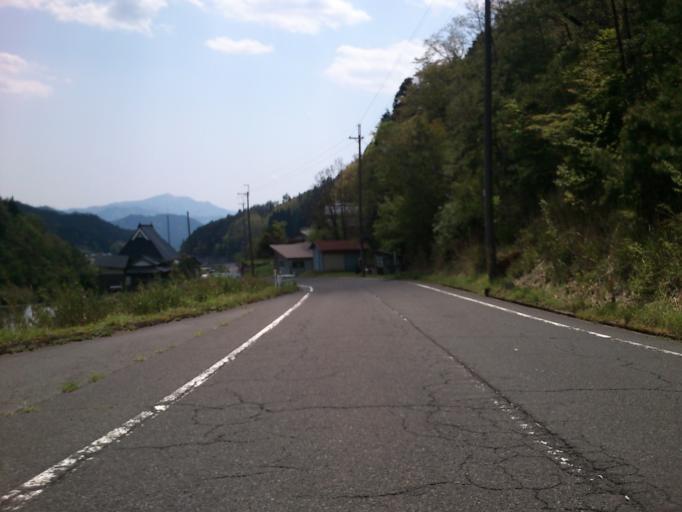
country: JP
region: Kyoto
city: Fukuchiyama
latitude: 35.3911
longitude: 134.9809
